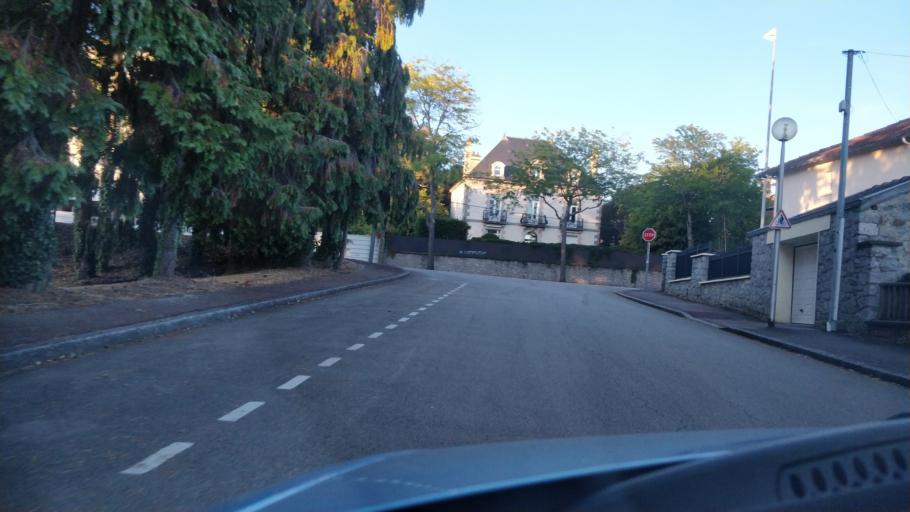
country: FR
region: Limousin
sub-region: Departement de la Haute-Vienne
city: Limoges
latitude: 45.8369
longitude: 1.2405
